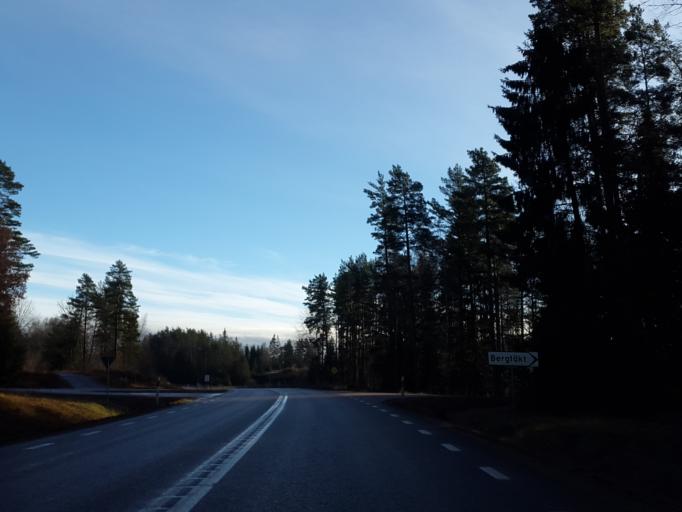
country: SE
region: Vaestra Goetaland
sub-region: Vargarda Kommun
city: Vargarda
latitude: 58.0480
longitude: 12.8573
